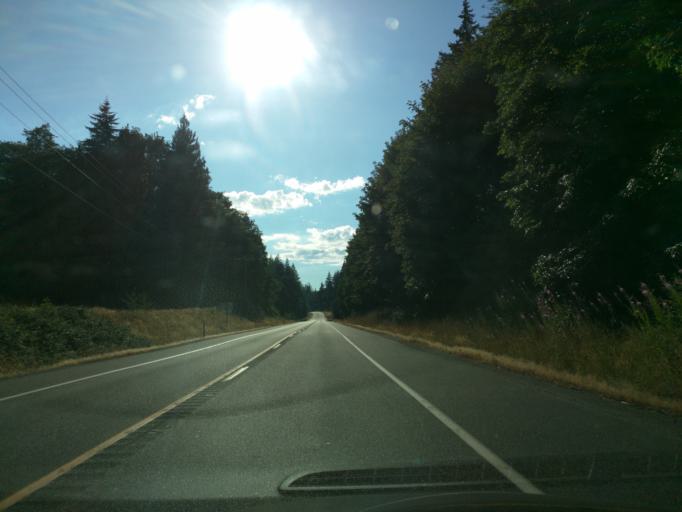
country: US
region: Washington
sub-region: Snohomish County
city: Darrington
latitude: 48.2771
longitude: -121.7511
